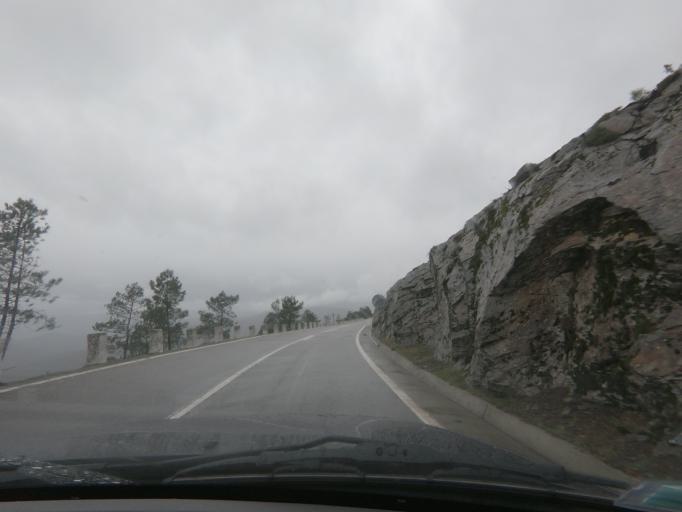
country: PT
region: Vila Real
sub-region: Mondim de Basto
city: Mondim de Basto
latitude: 41.3335
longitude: -7.8766
